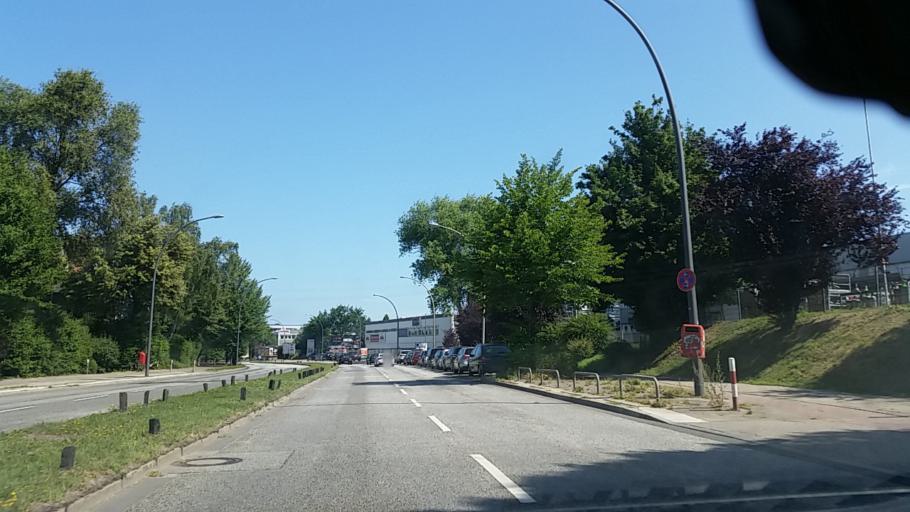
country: DE
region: Hamburg
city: Eidelstedt
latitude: 53.5892
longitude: 9.9046
